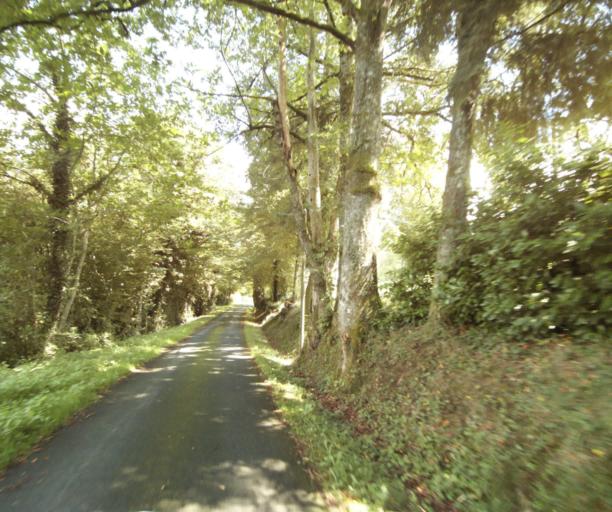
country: FR
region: Limousin
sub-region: Departement de la Correze
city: Sainte-Fortunade
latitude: 45.2055
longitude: 1.8377
